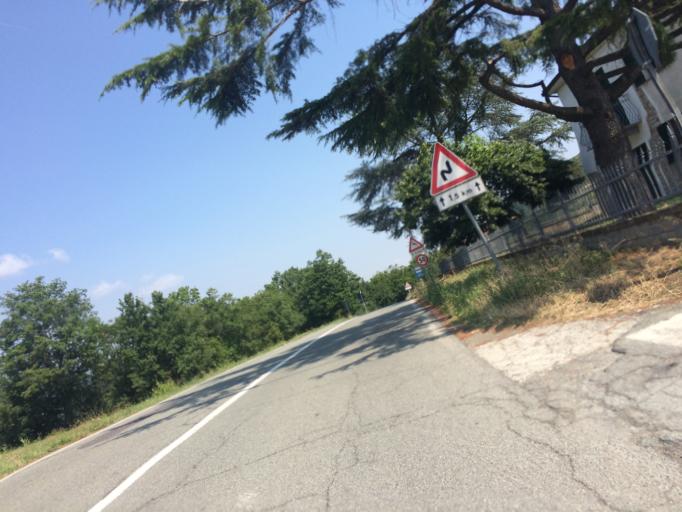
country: IT
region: Piedmont
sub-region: Provincia di Alessandria
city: Castelletto d'Erro
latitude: 44.6134
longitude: 8.4129
